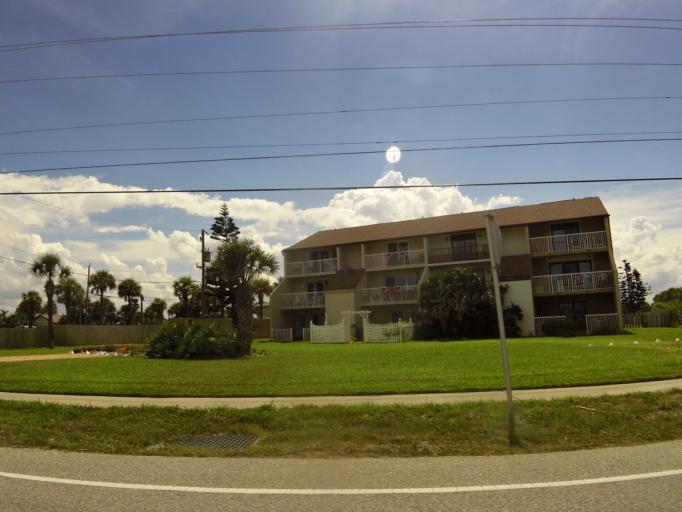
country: US
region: Florida
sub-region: Volusia County
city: Ormond-by-the-Sea
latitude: 29.3348
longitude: -81.0597
